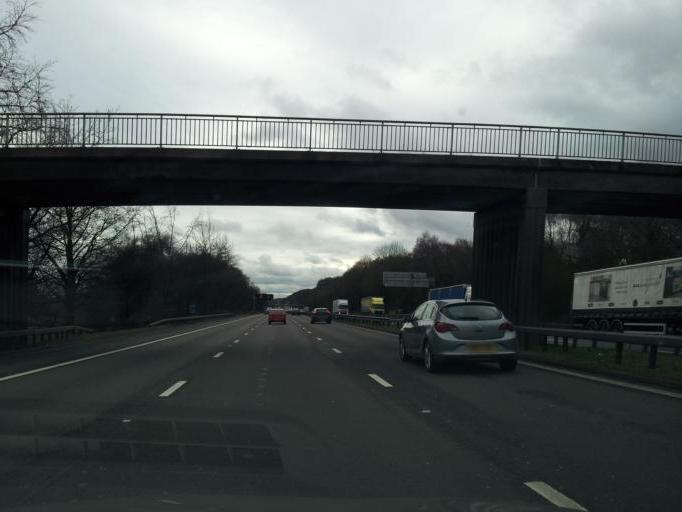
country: GB
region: England
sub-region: Staffordshire
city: Newcastle under Lyme
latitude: 52.9573
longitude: -2.2195
